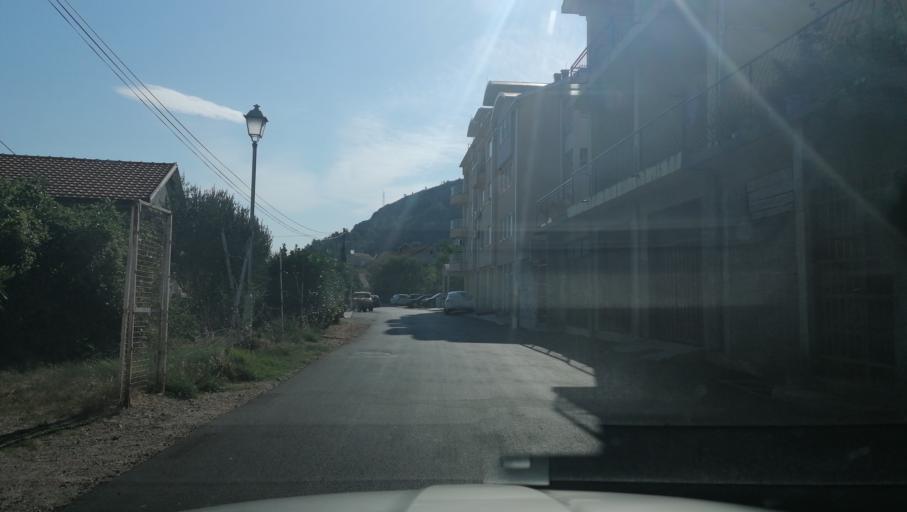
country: BA
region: Republika Srpska
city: Trebinje
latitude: 42.7138
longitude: 18.3528
